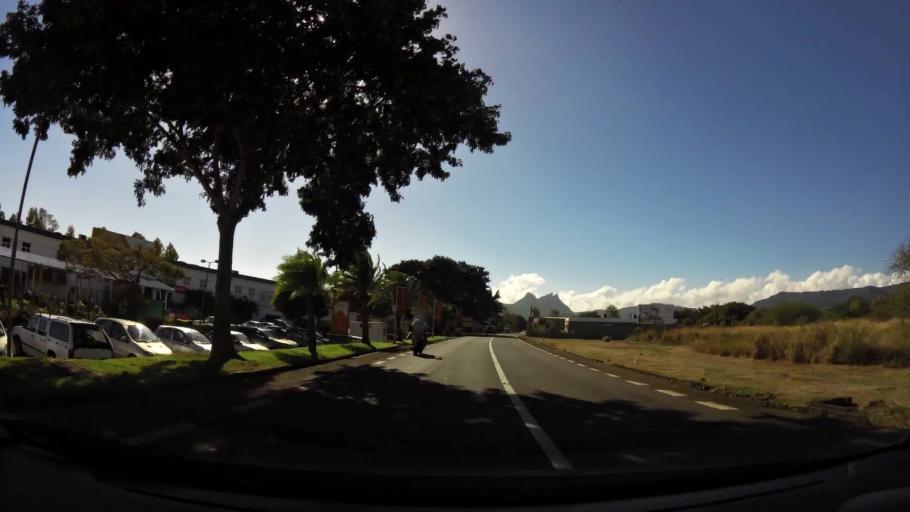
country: MU
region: Black River
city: Tamarin
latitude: -20.3279
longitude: 57.3845
